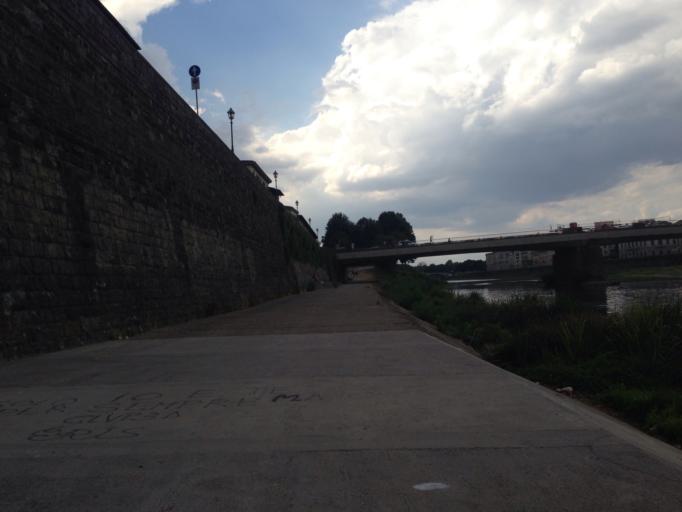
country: IT
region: Tuscany
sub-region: Province of Florence
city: Florence
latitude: 43.7708
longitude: 11.2441
